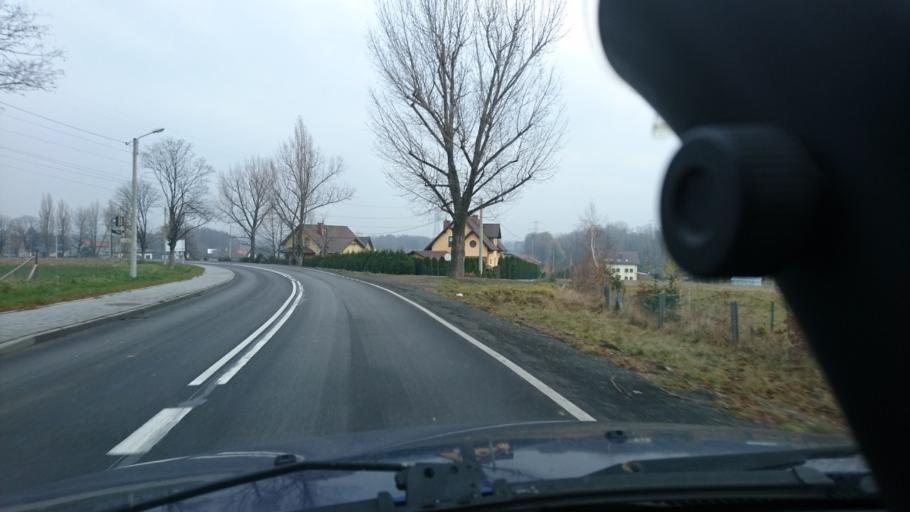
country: PL
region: Silesian Voivodeship
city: Janowice
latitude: 49.8631
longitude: 19.1160
